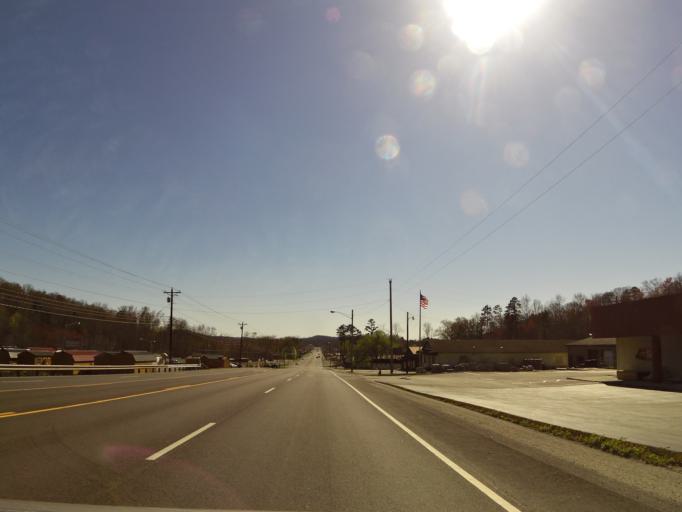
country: US
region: Tennessee
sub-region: Scott County
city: Oneida
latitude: 36.5215
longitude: -84.5005
